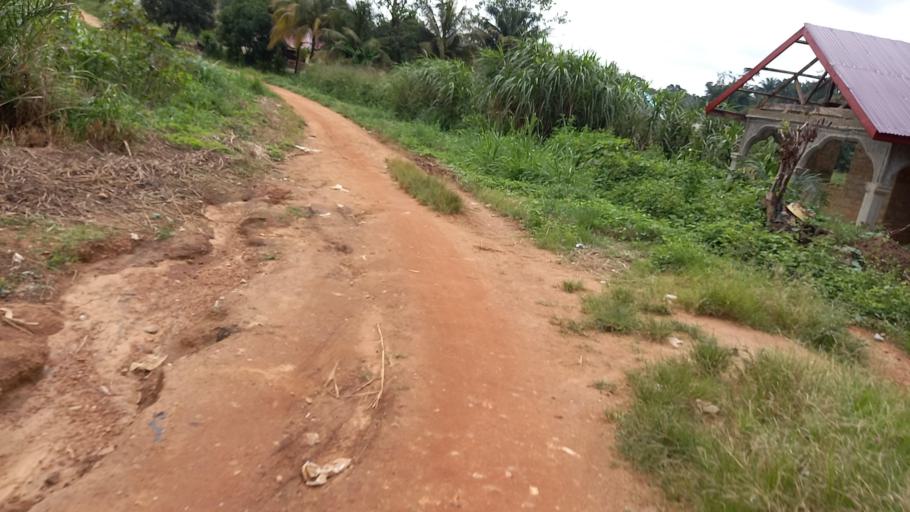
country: SL
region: Eastern Province
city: Kailahun
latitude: 8.2843
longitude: -10.5727
